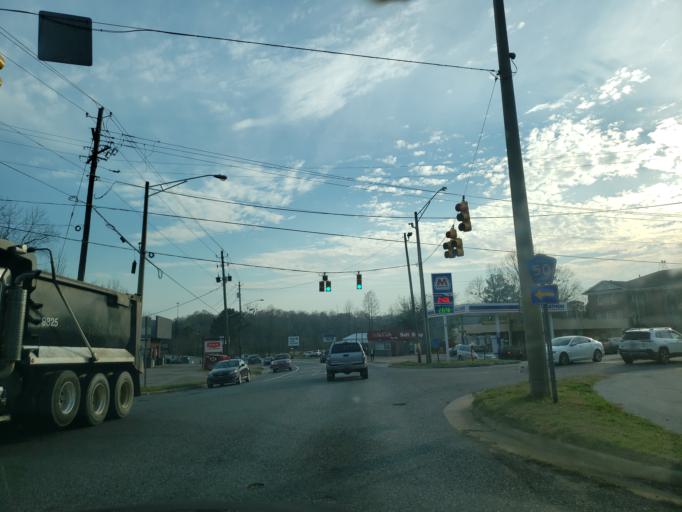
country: US
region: Alabama
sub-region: Hale County
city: Moundville
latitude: 32.9974
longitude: -87.6234
